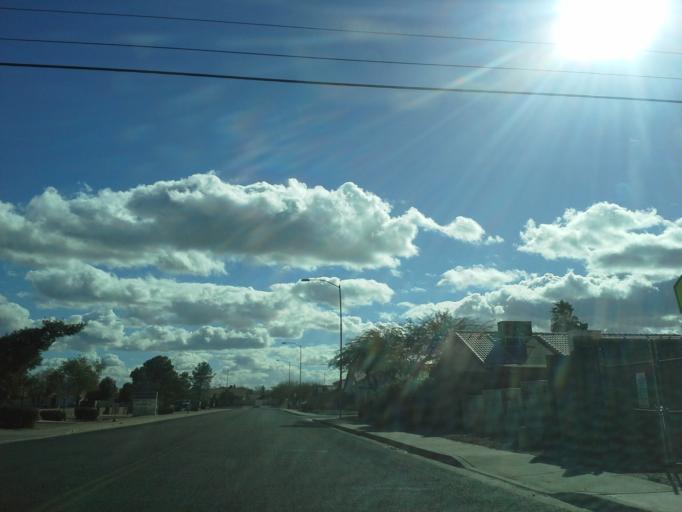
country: US
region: Arizona
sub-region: Maricopa County
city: Gilbert
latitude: 33.4013
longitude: -111.7140
